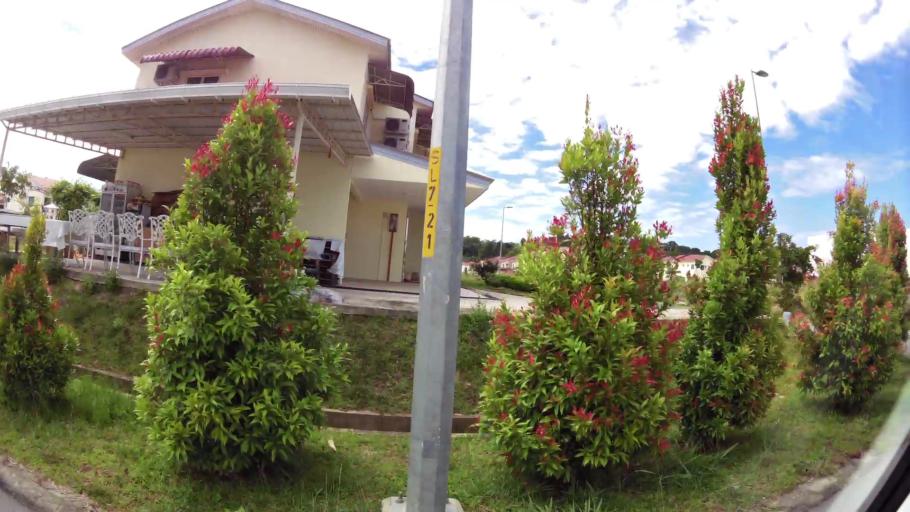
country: BN
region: Brunei and Muara
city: Bandar Seri Begawan
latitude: 4.9734
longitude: 115.0049
